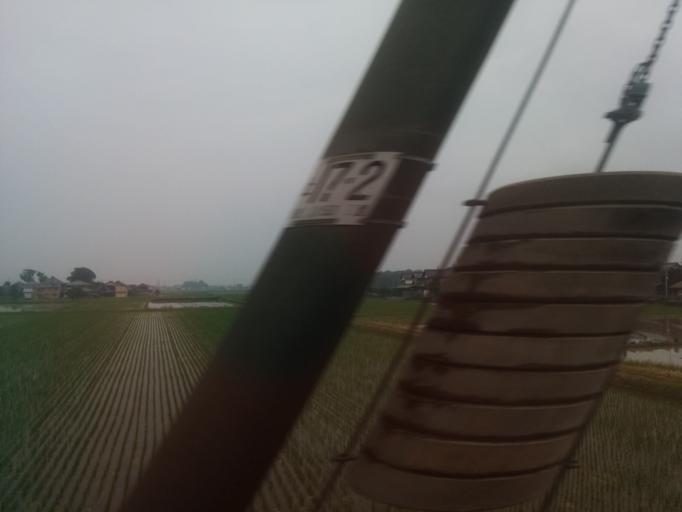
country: JP
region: Shiga Prefecture
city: Hikone
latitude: 35.2367
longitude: 136.2378
